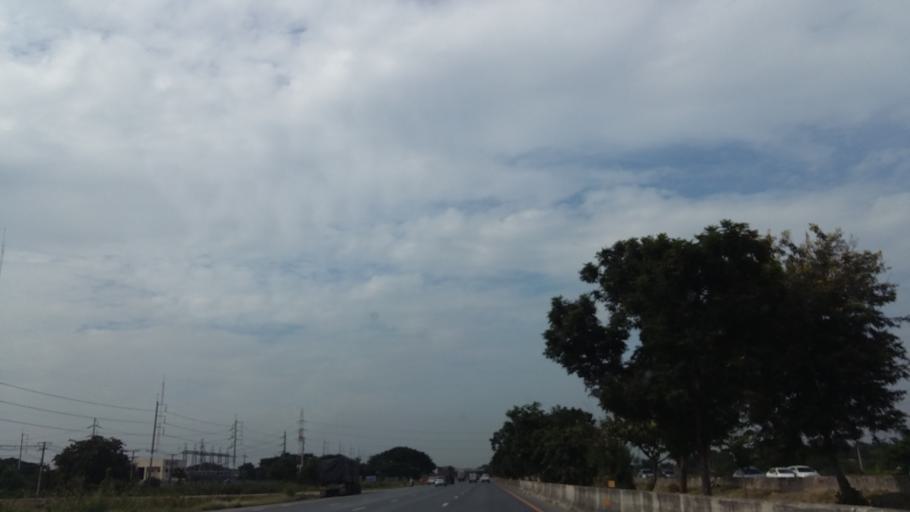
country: TH
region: Phra Nakhon Si Ayutthaya
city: Maha Rat
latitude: 14.5018
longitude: 100.5211
